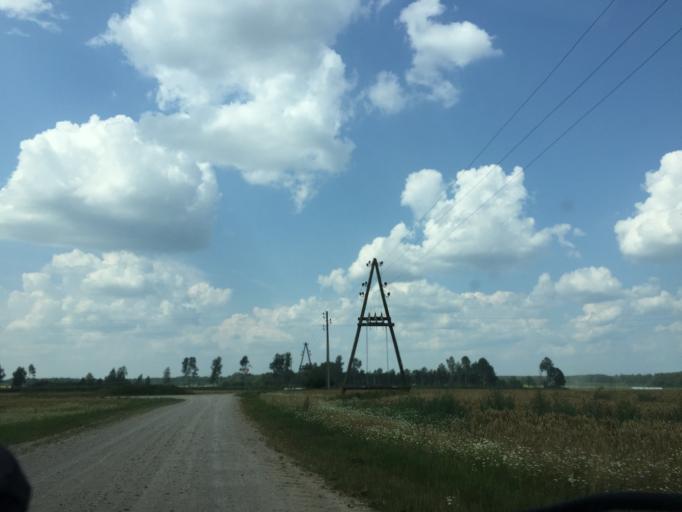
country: LT
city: Zagare
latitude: 56.3457
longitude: 23.1425
